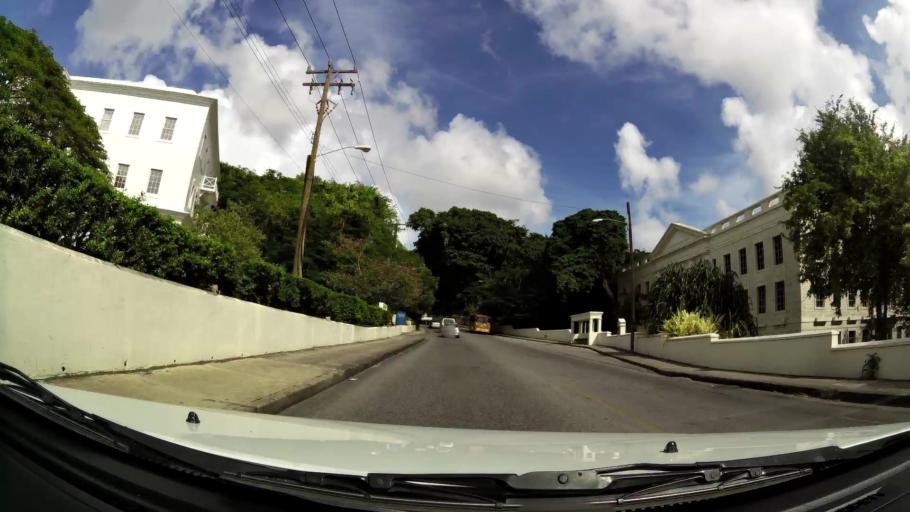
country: BB
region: Saint Michael
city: Bridgetown
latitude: 13.0930
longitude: -59.6012
